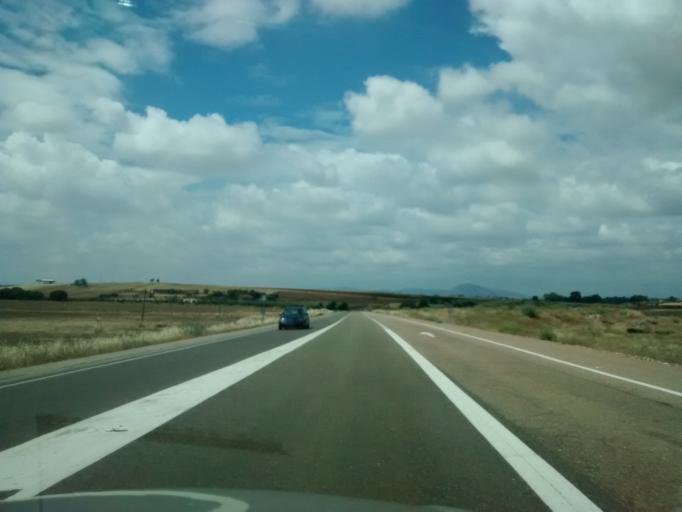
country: ES
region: Extremadura
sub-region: Provincia de Badajoz
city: Trujillanos
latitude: 38.9440
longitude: -6.2894
